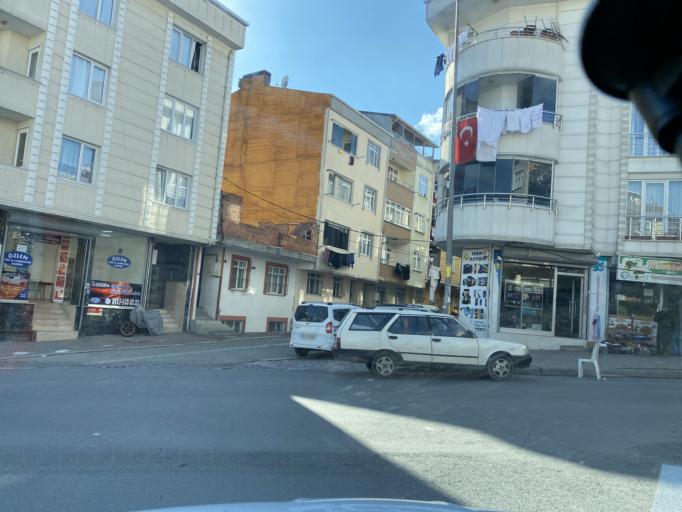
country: TR
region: Istanbul
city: Esenyurt
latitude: 41.0290
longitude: 28.6520
